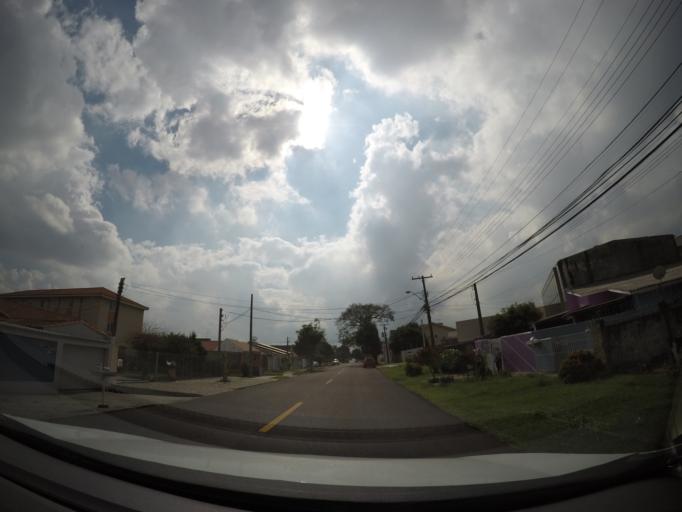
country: BR
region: Parana
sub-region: Sao Jose Dos Pinhais
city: Sao Jose dos Pinhais
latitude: -25.4907
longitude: -49.2468
